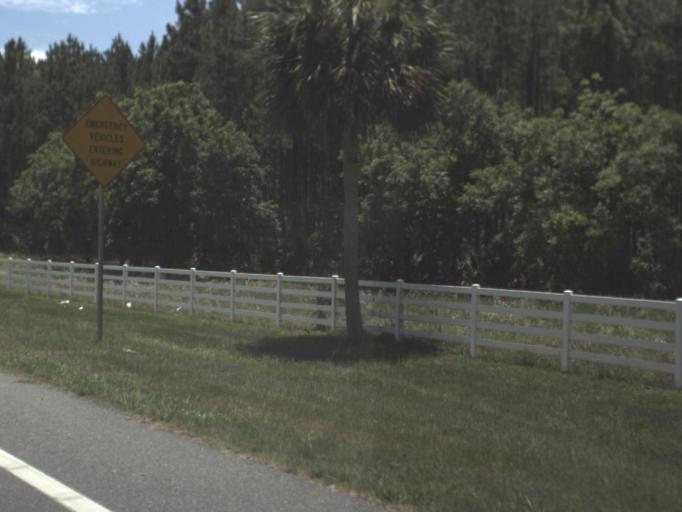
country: US
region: Florida
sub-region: Levy County
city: Manatee Road
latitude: 29.6078
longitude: -82.9825
